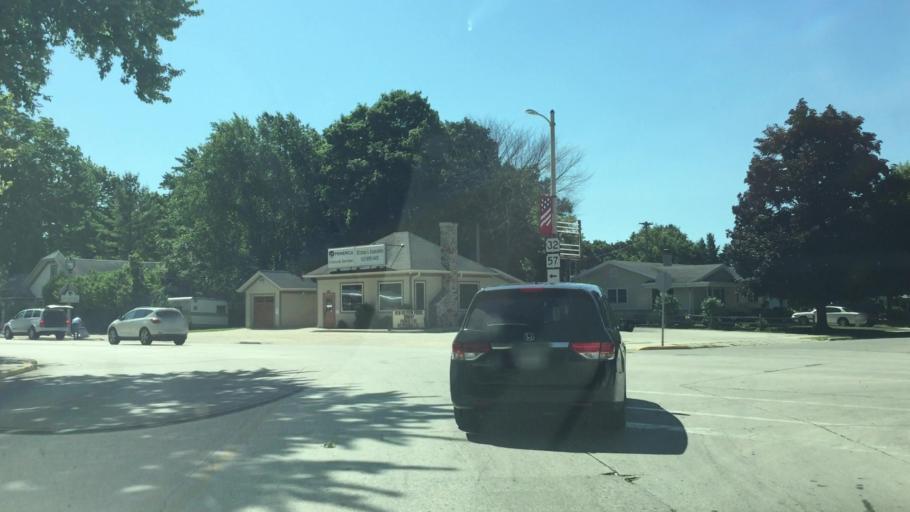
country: US
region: Wisconsin
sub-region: Calumet County
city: New Holstein
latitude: 43.9499
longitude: -88.0984
